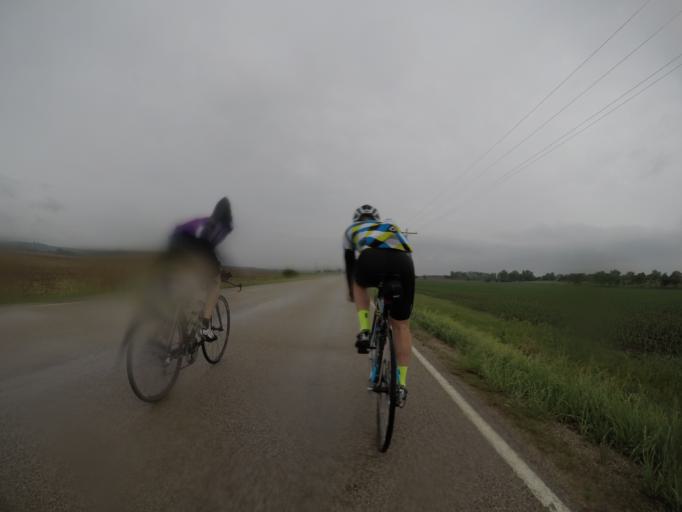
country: US
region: Kansas
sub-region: Pottawatomie County
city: Wamego
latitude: 39.3303
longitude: -96.2214
